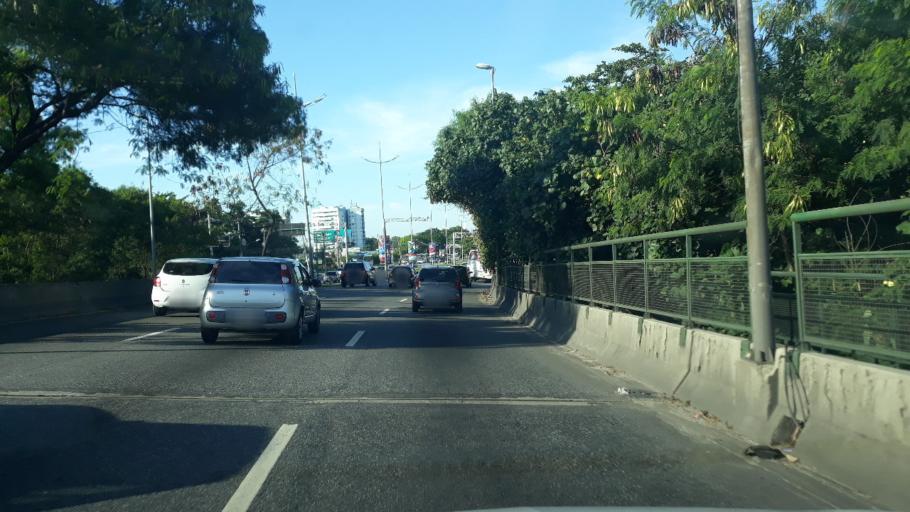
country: BR
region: Rio de Janeiro
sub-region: Rio De Janeiro
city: Rio de Janeiro
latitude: -22.9674
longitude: -43.3577
